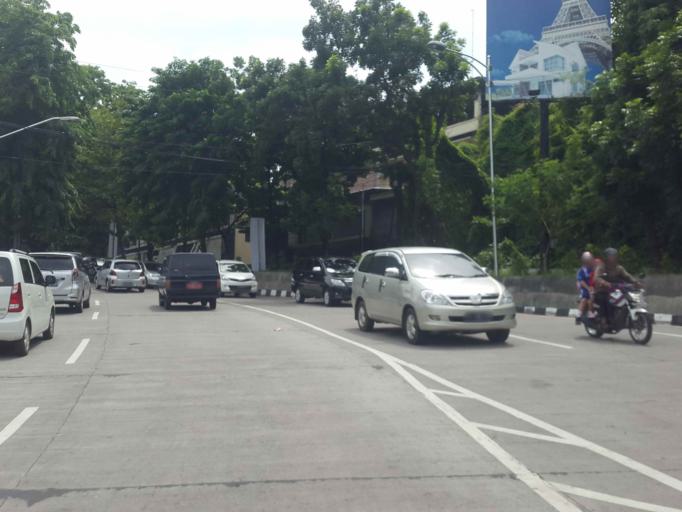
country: ID
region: Central Java
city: Semarang
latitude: -6.9979
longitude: 110.4193
